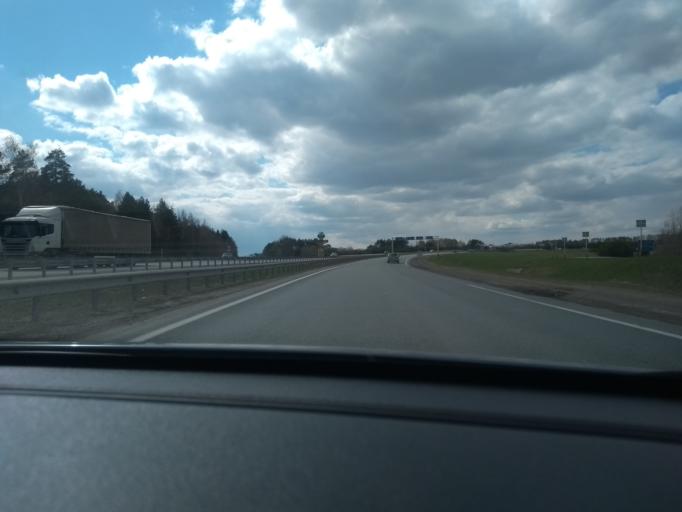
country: RU
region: Tatarstan
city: Yelabuga
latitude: 55.7815
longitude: 52.1838
